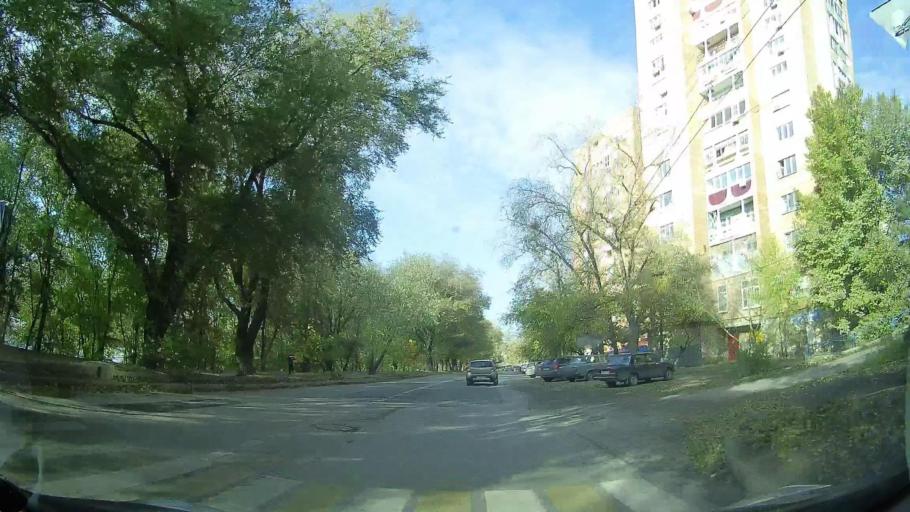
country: RU
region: Rostov
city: Severnyy
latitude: 47.2784
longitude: 39.7070
